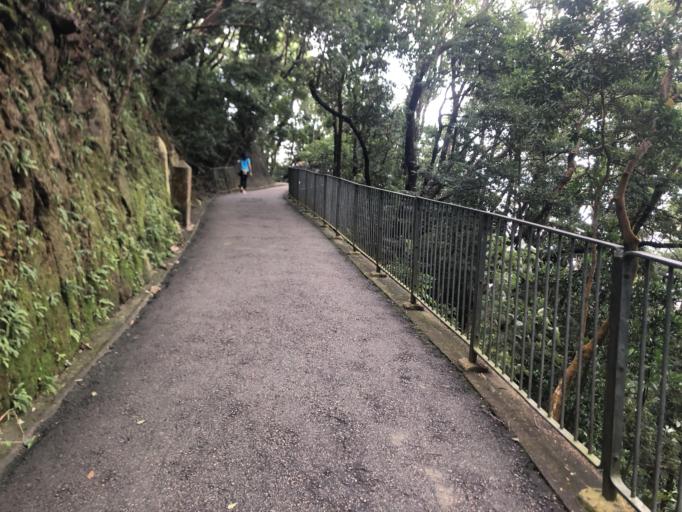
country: HK
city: Hong Kong
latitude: 22.2790
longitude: 114.1376
